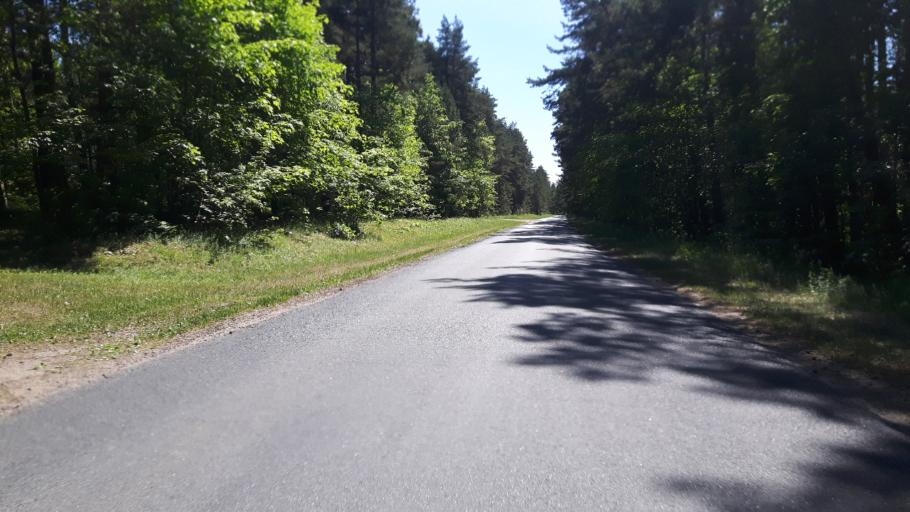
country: LV
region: Salacgrivas
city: Ainazi
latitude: 57.9115
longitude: 24.3834
